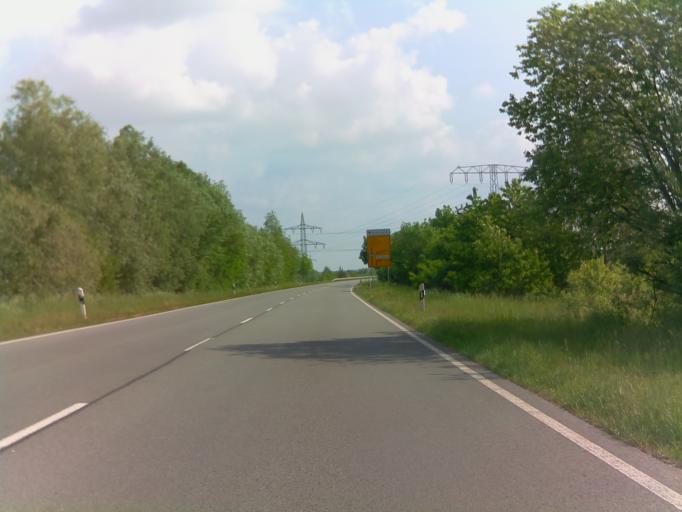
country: DE
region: Saxony-Anhalt
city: Gardelegen
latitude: 52.5311
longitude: 11.3660
